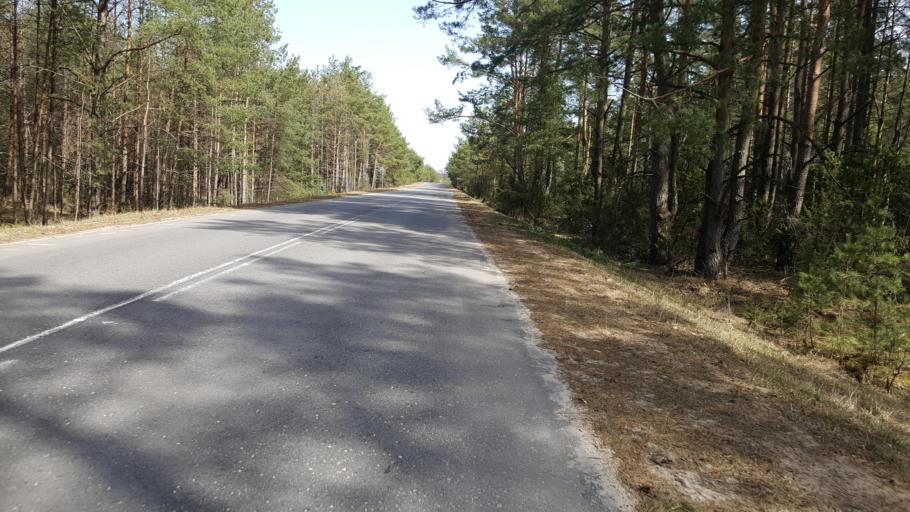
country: BY
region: Brest
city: Kamyanyuki
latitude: 52.5277
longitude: 23.8307
